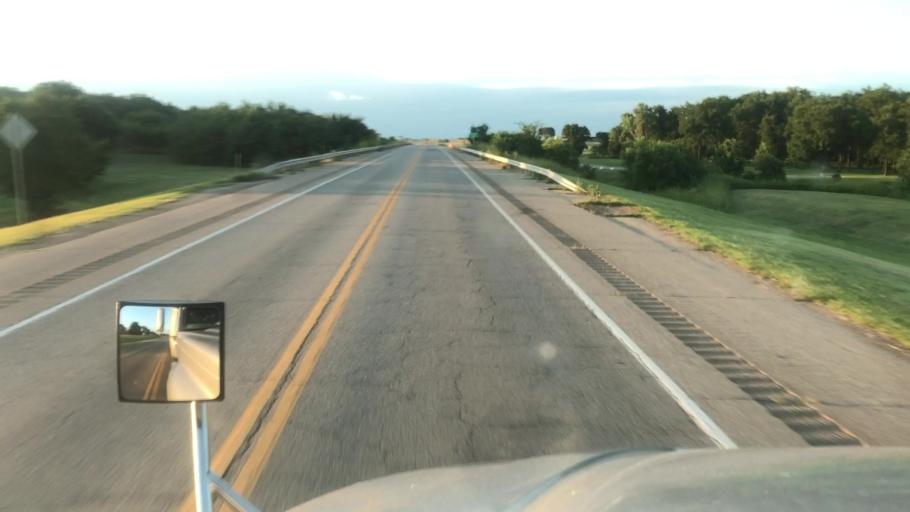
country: US
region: Oklahoma
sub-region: Osage County
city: McCord
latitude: 36.4929
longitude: -97.0736
